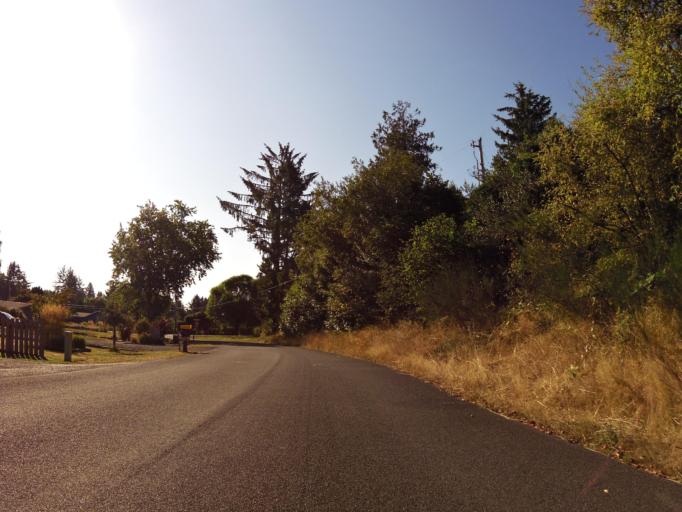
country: US
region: Oregon
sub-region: Clatsop County
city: Warrenton
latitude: 46.1335
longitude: -123.9336
